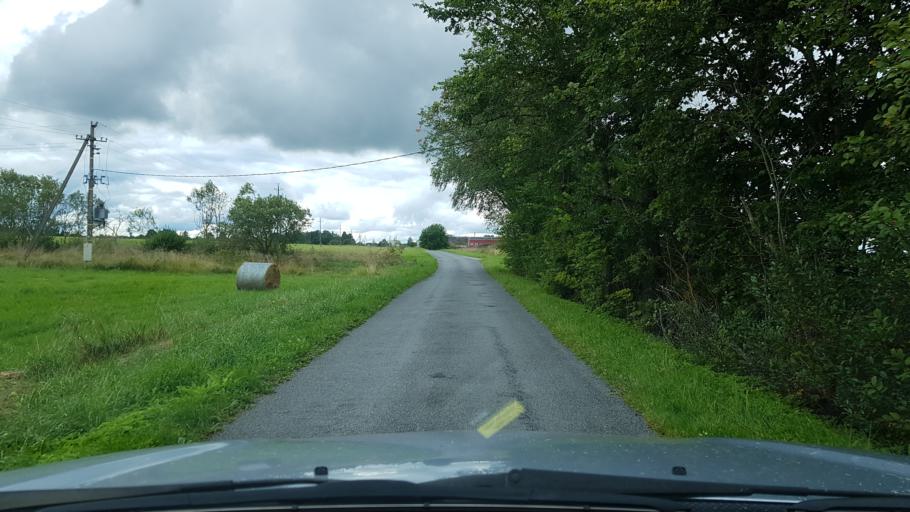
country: EE
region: Harju
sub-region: Rae vald
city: Vaida
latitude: 59.2944
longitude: 24.9866
